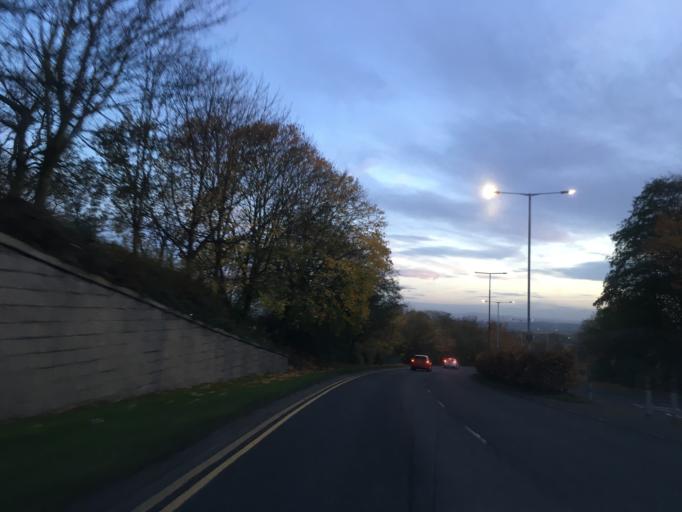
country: GB
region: Scotland
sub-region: Fife
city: Dunfermline
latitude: 56.0720
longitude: -3.4517
